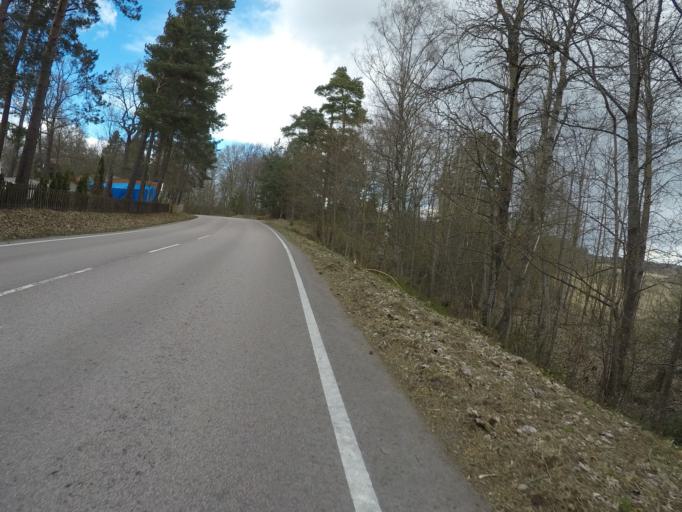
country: SE
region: Soedermanland
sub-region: Eskilstuna Kommun
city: Kvicksund
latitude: 59.4759
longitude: 16.2881
